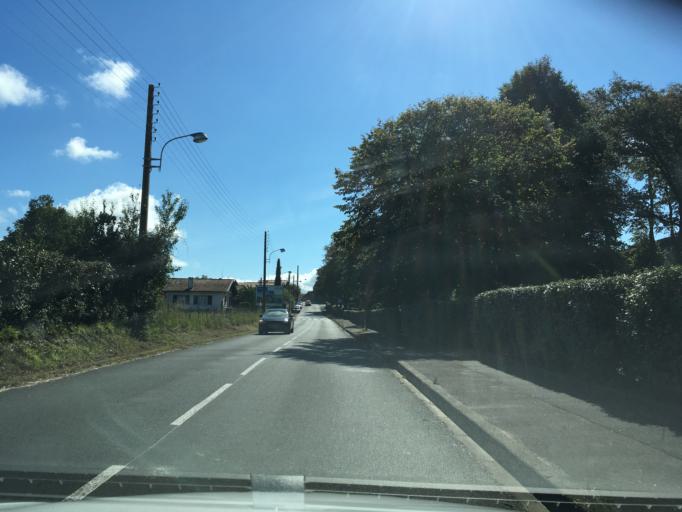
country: FR
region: Aquitaine
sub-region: Departement des Pyrenees-Atlantiques
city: Bayonne
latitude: 43.5064
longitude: -1.4776
